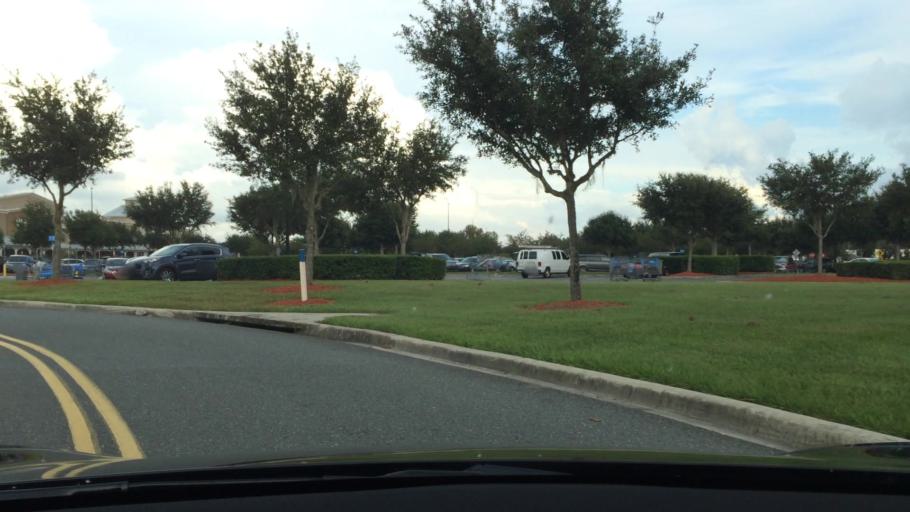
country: US
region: Florida
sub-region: Hillsborough County
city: Lutz
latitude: 28.1789
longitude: -82.4685
